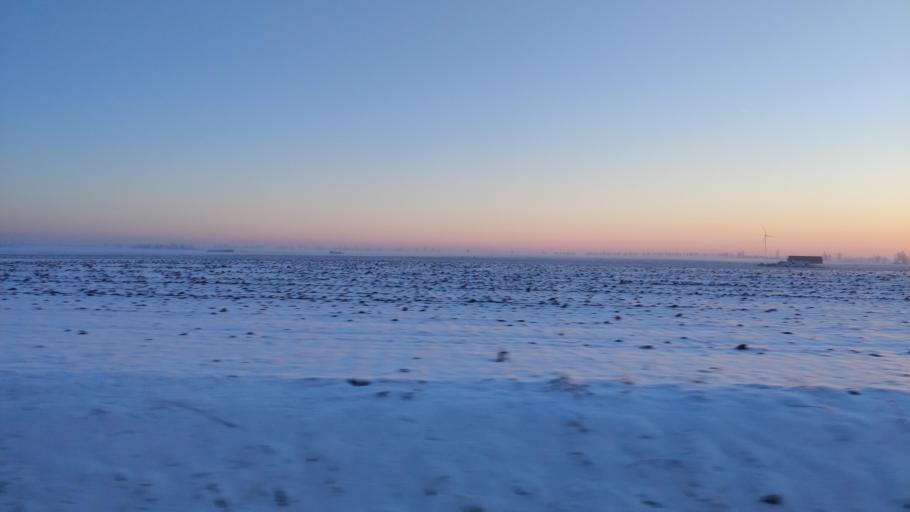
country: PL
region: Kujawsko-Pomorskie
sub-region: Powiat zninski
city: Znin
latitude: 52.8691
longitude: 17.8054
